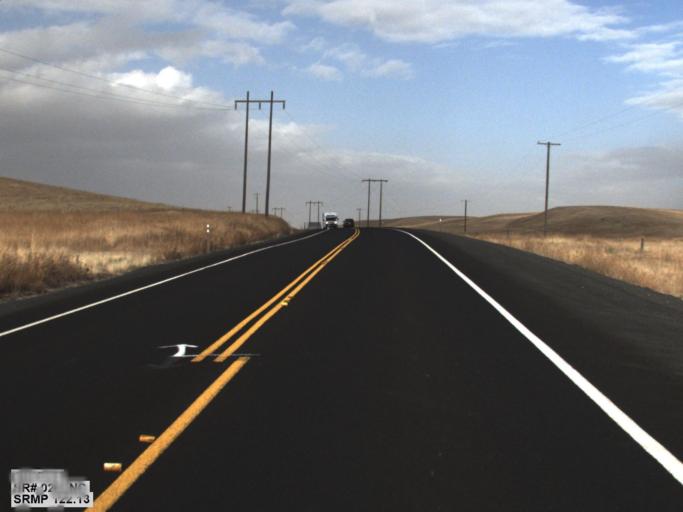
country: US
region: Washington
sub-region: Lincoln County
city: Davenport
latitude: 47.5309
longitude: -118.2012
